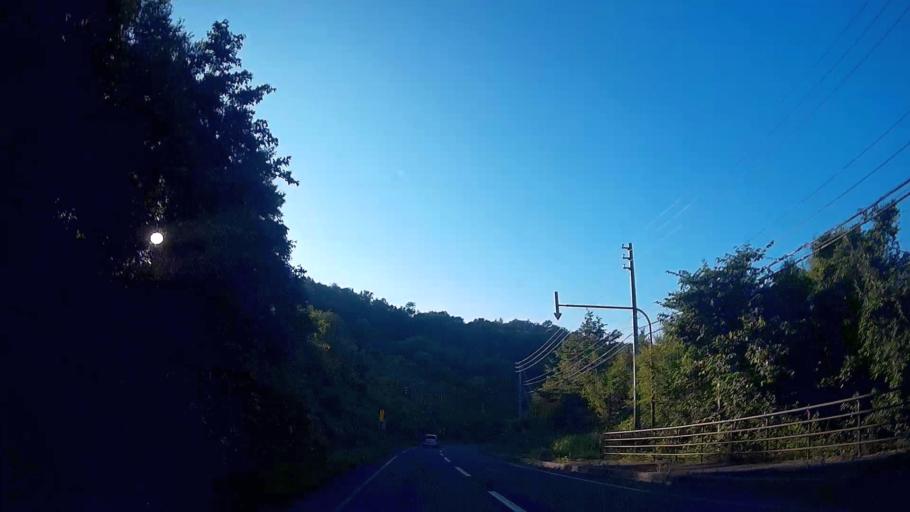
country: JP
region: Hokkaido
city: Date
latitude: 42.6473
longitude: 140.8149
